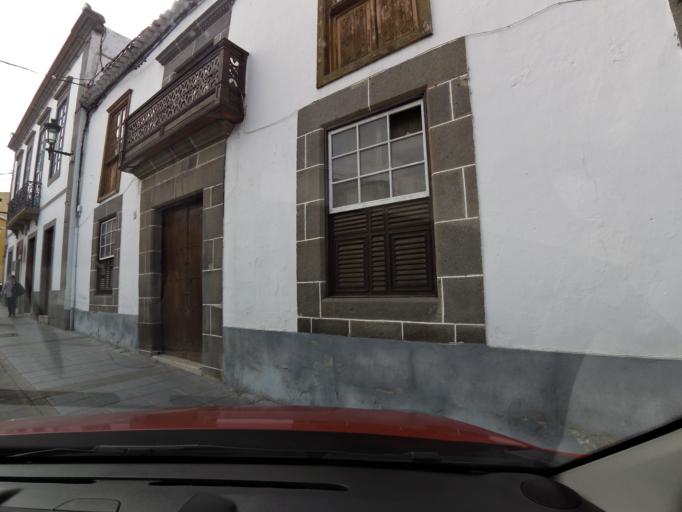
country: ES
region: Canary Islands
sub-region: Provincia de Las Palmas
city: Telde
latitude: 28.0032
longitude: -15.4145
